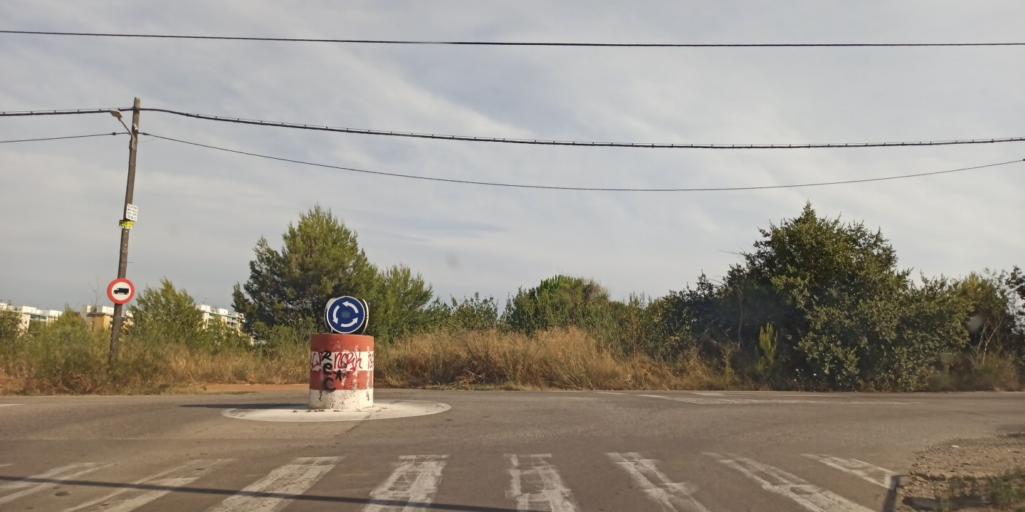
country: ES
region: Catalonia
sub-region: Provincia de Barcelona
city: Santa Coloma de Cervello
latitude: 41.3598
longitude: 2.0252
